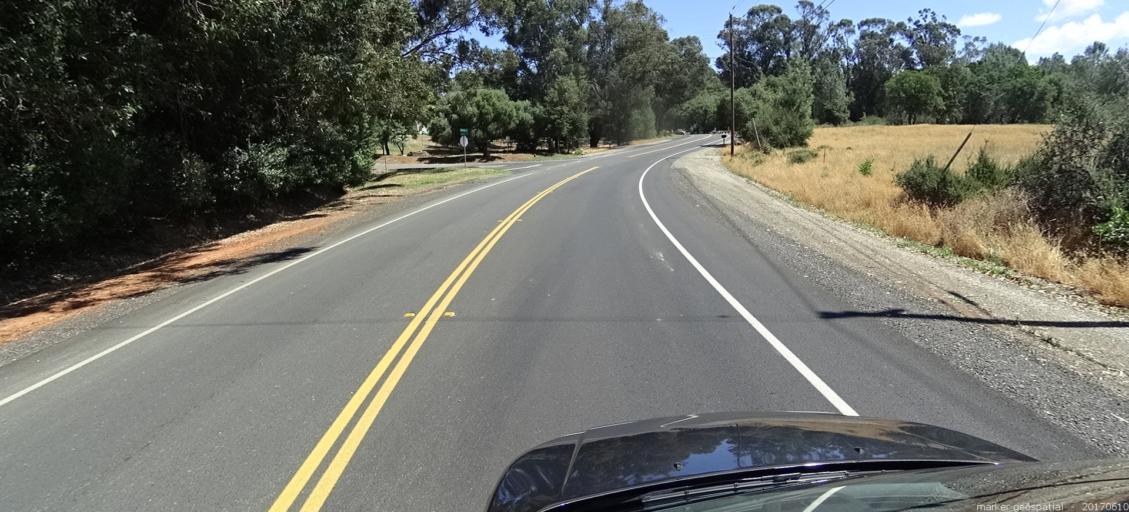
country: US
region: California
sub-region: Butte County
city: Oroville East
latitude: 39.5239
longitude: -121.4826
